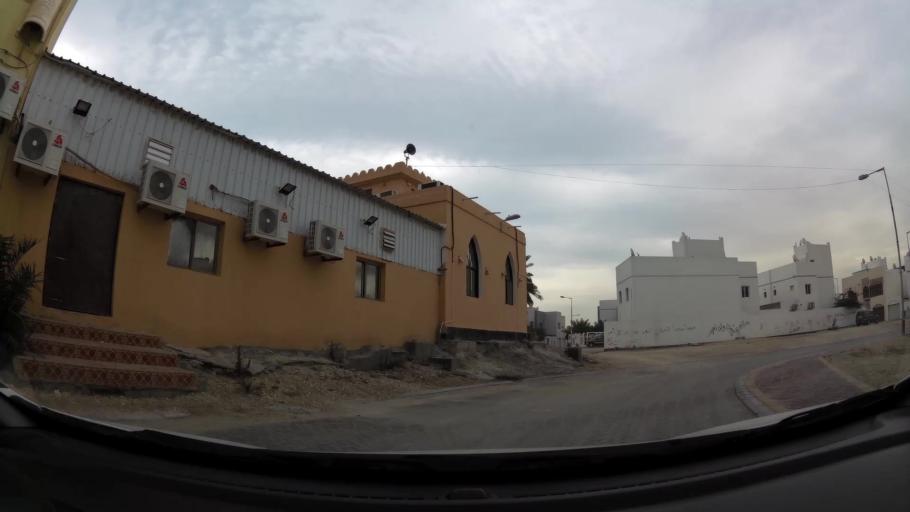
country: BH
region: Northern
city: Madinat `Isa
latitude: 26.1807
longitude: 50.5817
